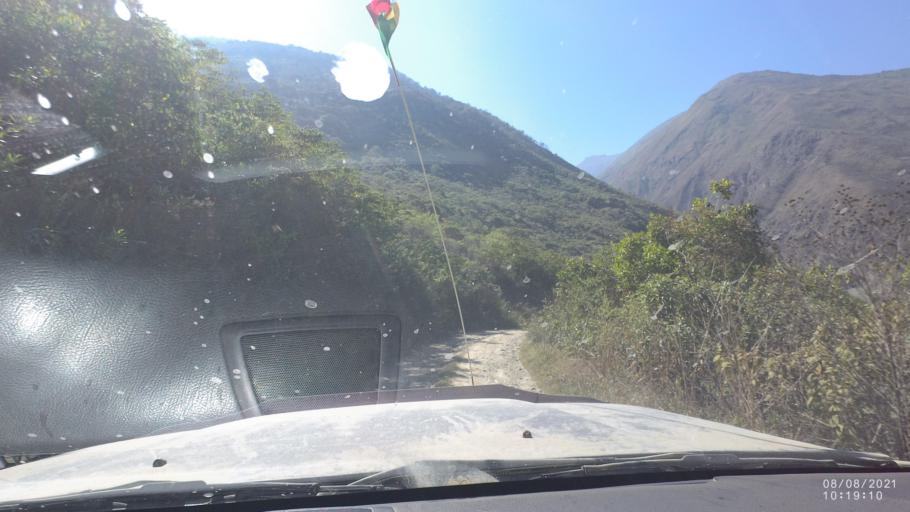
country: BO
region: La Paz
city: Quime
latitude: -16.6862
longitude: -66.7273
